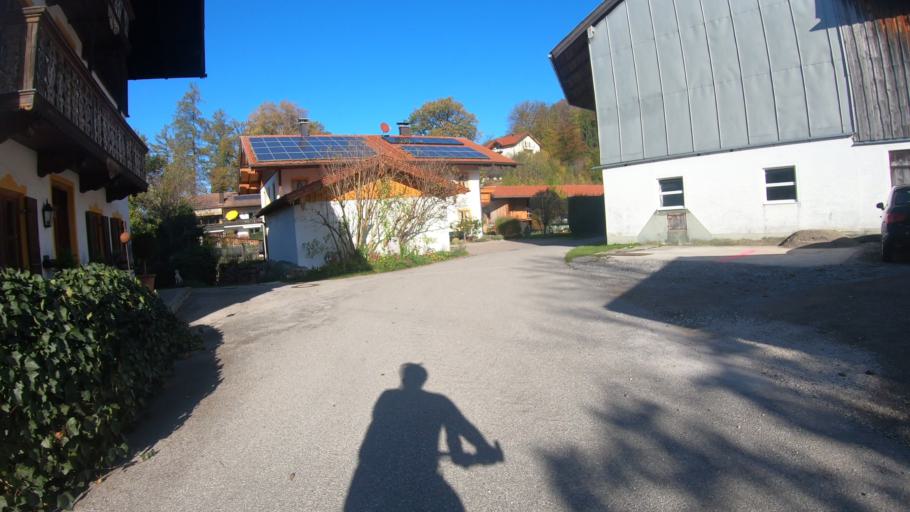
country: DE
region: Bavaria
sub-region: Upper Bavaria
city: Bergen
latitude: 47.8071
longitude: 12.5914
